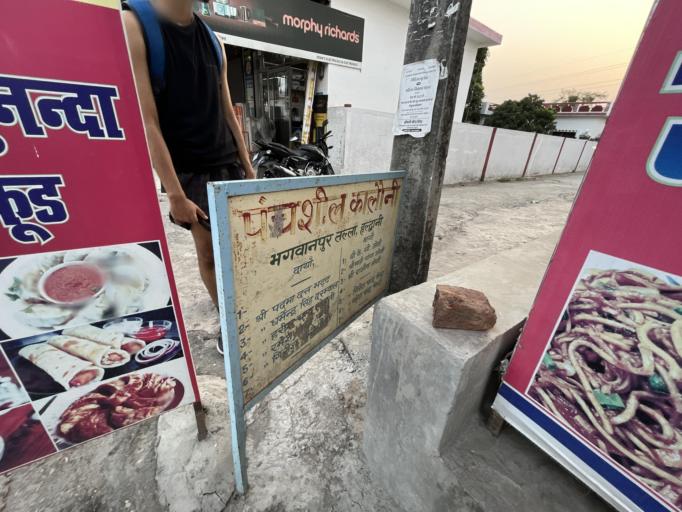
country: IN
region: Uttarakhand
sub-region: Naini Tal
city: Haldwani
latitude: 29.2171
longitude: 79.4732
